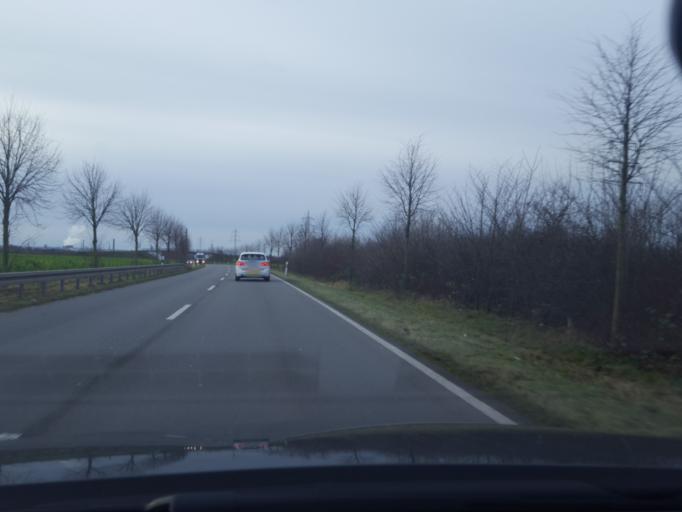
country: DE
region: North Rhine-Westphalia
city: Niederkassel
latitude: 50.8302
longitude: 7.0612
